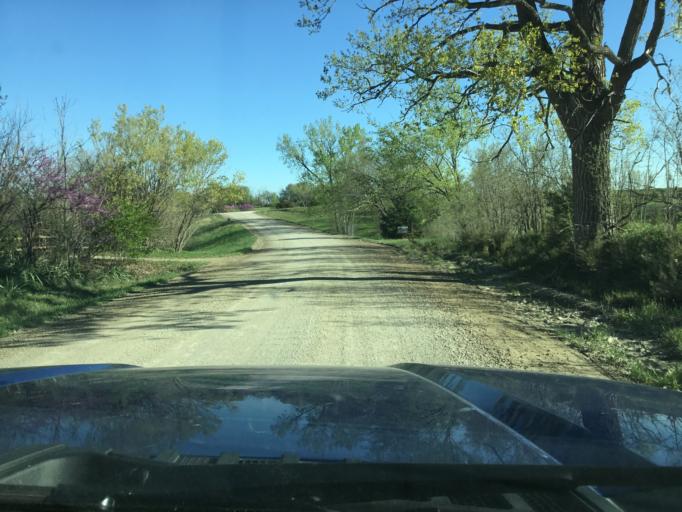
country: US
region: Kansas
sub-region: Douglas County
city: Lawrence
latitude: 38.9696
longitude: -95.3725
